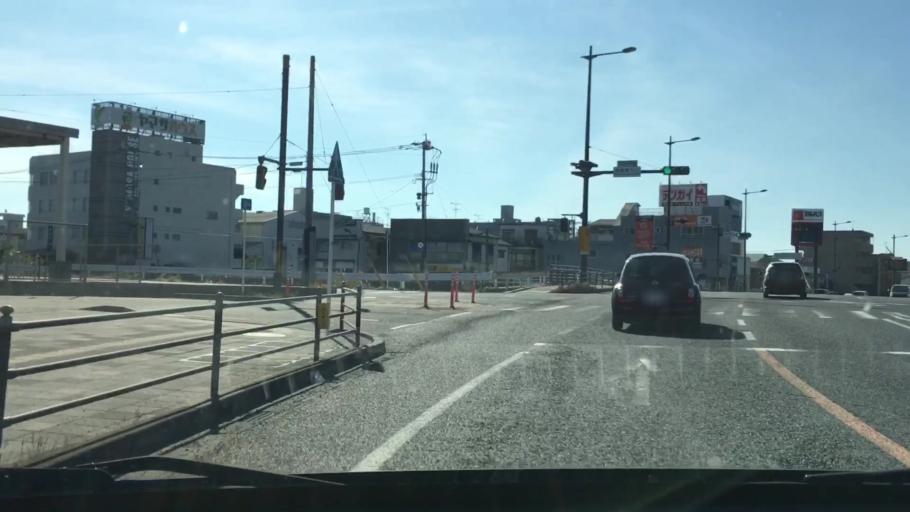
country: JP
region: Kagoshima
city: Kagoshima-shi
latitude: 31.5792
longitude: 130.5626
